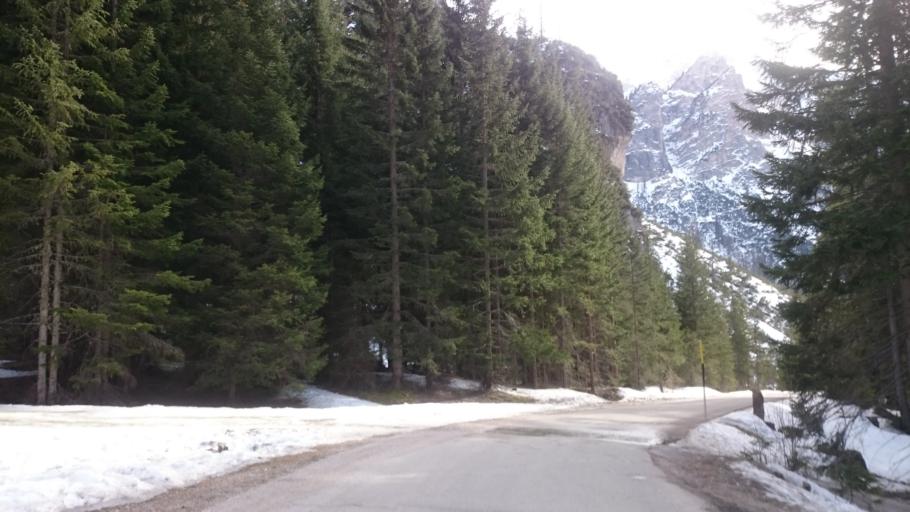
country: IT
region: Trentino-Alto Adige
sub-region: Bolzano
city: Braies
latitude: 46.6718
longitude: 12.1515
